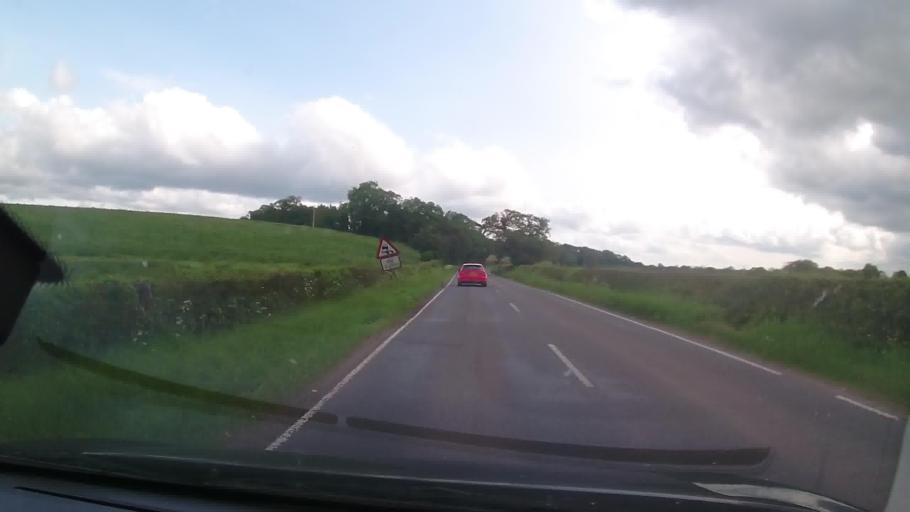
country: GB
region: England
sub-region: Shropshire
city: Wem
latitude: 52.8345
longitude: -2.7323
